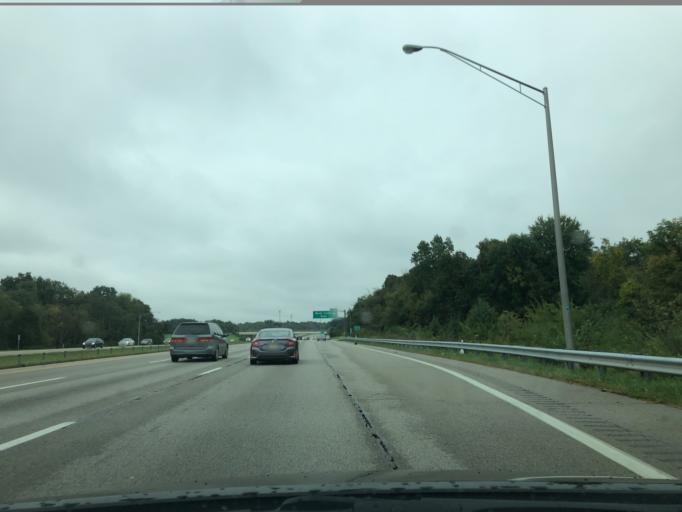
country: US
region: Ohio
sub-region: Hamilton County
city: The Village of Indian Hill
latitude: 39.2288
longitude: -84.2849
